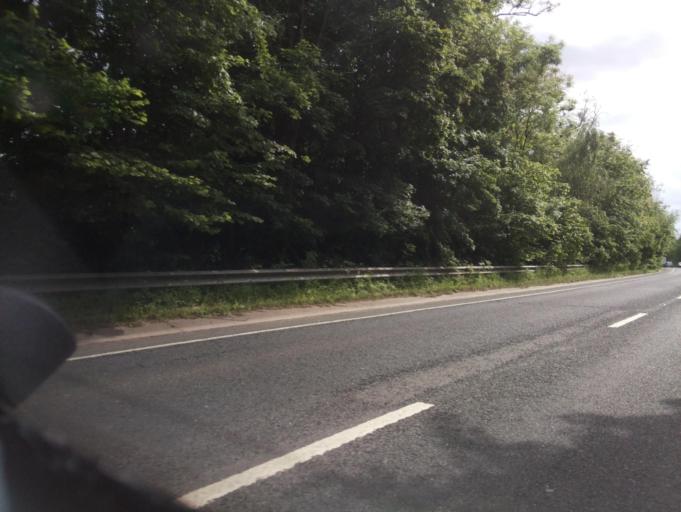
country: GB
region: England
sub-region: Worcestershire
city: Bransford
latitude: 52.1863
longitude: -2.2718
